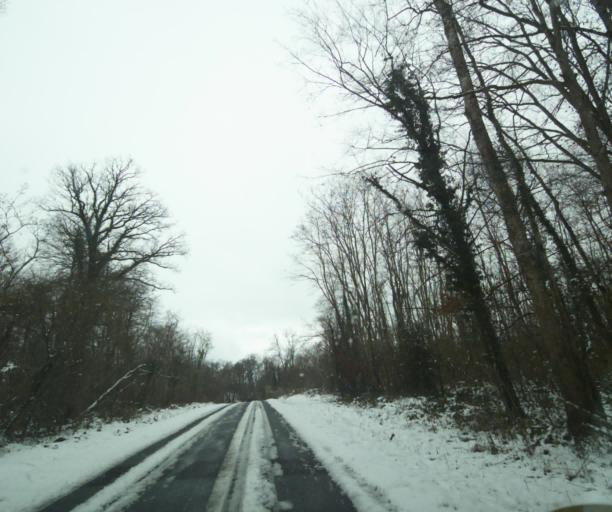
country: FR
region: Champagne-Ardenne
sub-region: Departement de la Haute-Marne
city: Montier-en-Der
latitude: 48.4226
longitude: 4.7284
